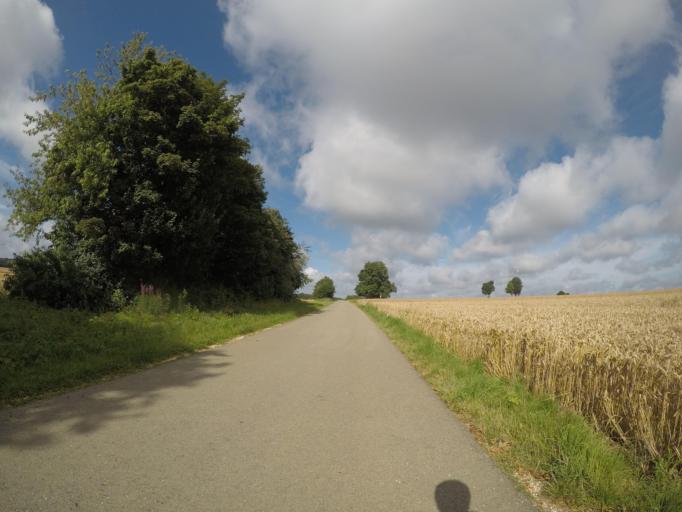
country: DE
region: Baden-Wuerttemberg
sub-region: Tuebingen Region
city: Laichingen
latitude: 48.4458
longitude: 9.6410
